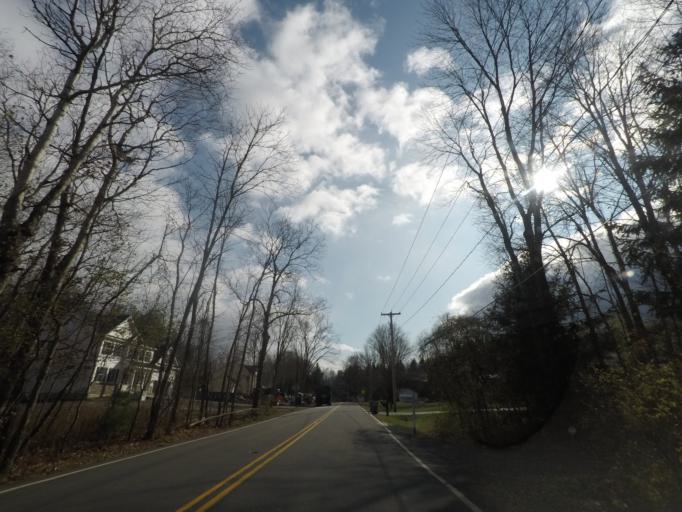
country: US
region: New York
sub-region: Saratoga County
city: Country Knolls
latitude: 42.9178
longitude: -73.8335
